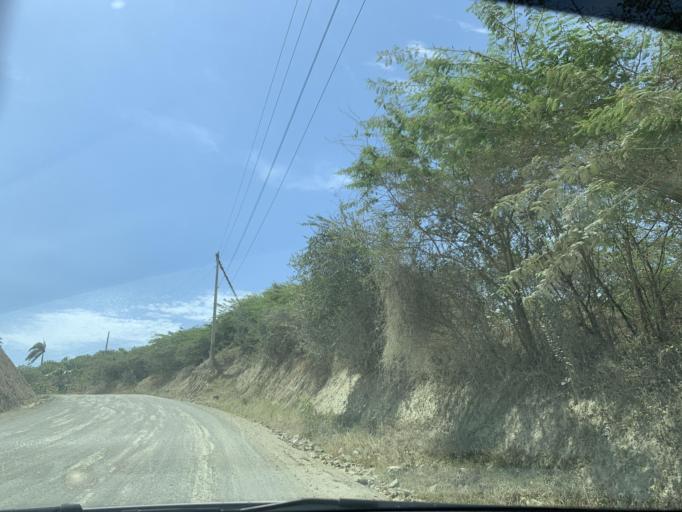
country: DO
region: Puerto Plata
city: Imbert
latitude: 19.8662
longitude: -70.8128
